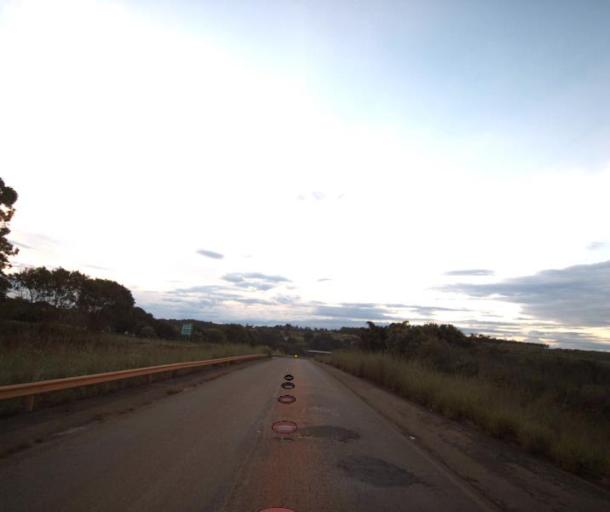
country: BR
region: Goias
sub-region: Anapolis
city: Anapolis
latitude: -16.2471
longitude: -48.9998
